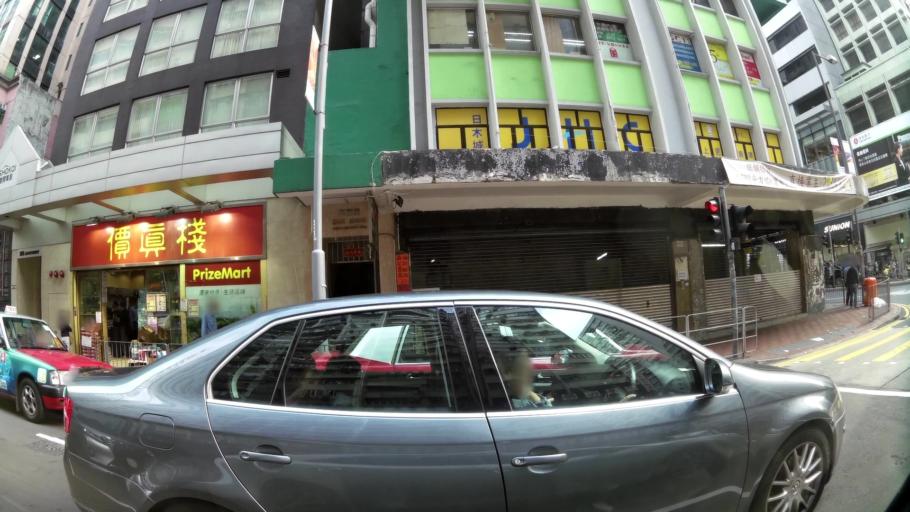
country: HK
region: Wanchai
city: Wan Chai
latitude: 22.2778
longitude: 114.1750
